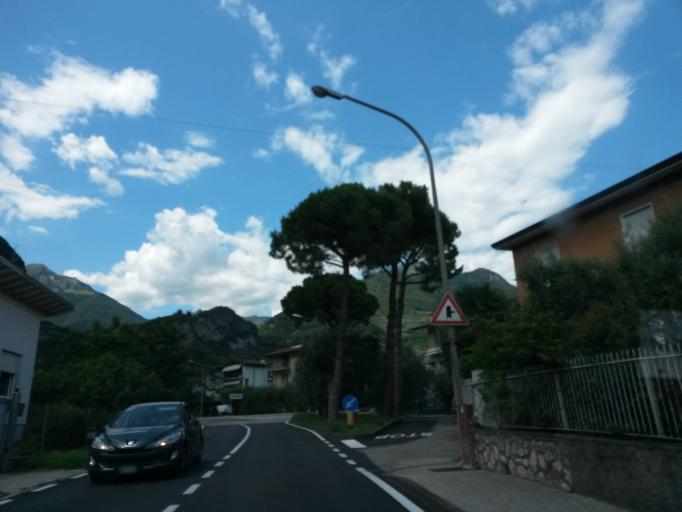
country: IT
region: Trentino-Alto Adige
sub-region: Provincia di Trento
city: Riva del Garda
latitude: 45.9032
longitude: 10.8434
